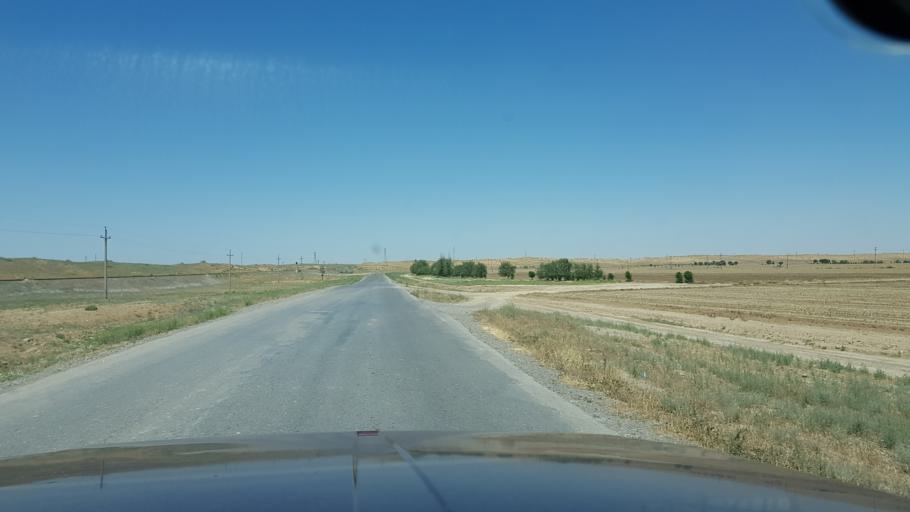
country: TM
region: Ahal
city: Annau
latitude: 37.8506
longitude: 58.7125
